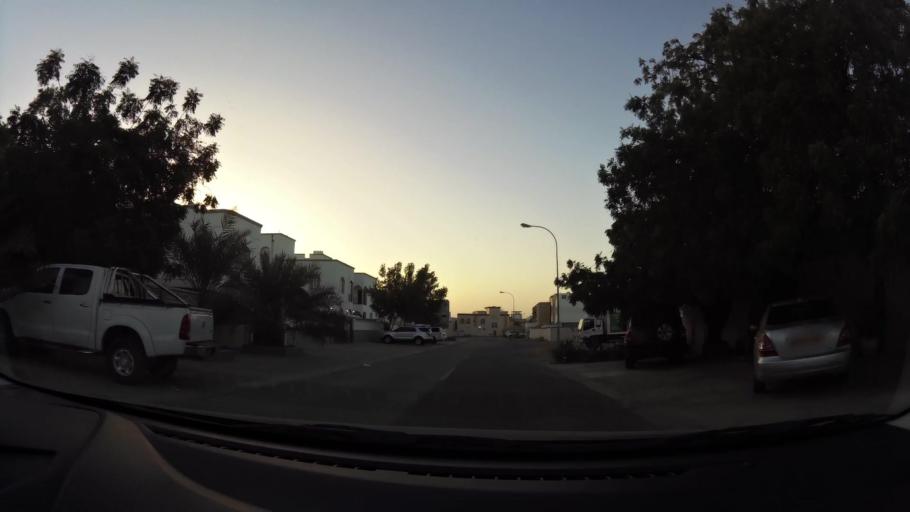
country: OM
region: Muhafazat Masqat
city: As Sib al Jadidah
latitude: 23.5966
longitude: 58.2378
